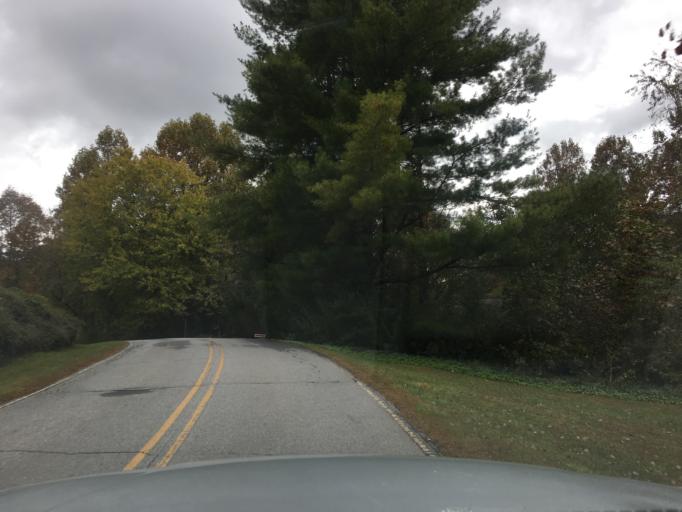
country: US
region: North Carolina
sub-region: Henderson County
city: Laurel Park
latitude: 35.3004
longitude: -82.5063
